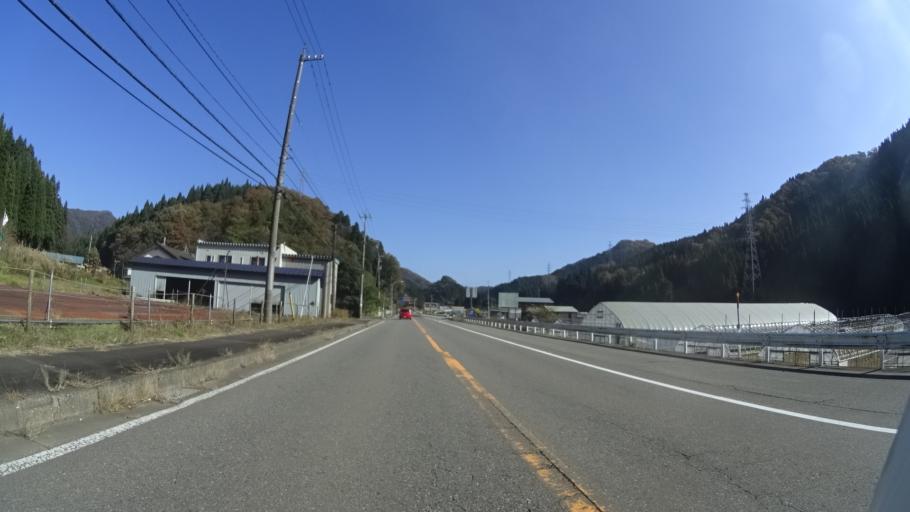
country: JP
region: Fukui
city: Ono
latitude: 35.9989
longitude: 136.4240
